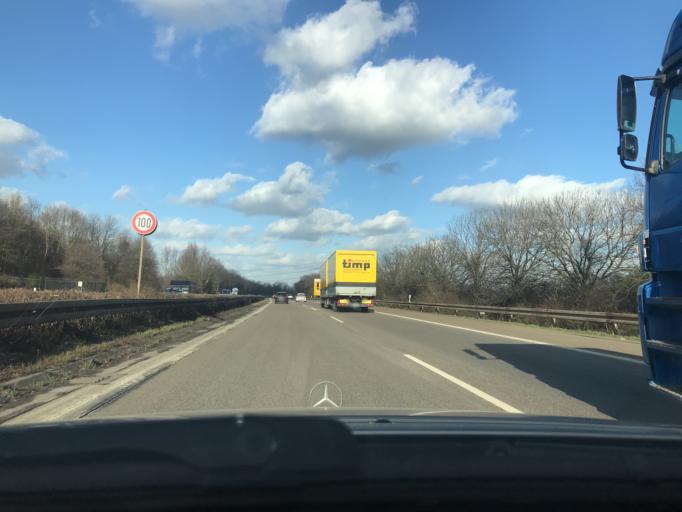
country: DE
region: North Rhine-Westphalia
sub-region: Regierungsbezirk Dusseldorf
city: Krefeld
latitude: 51.3763
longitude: 6.6417
